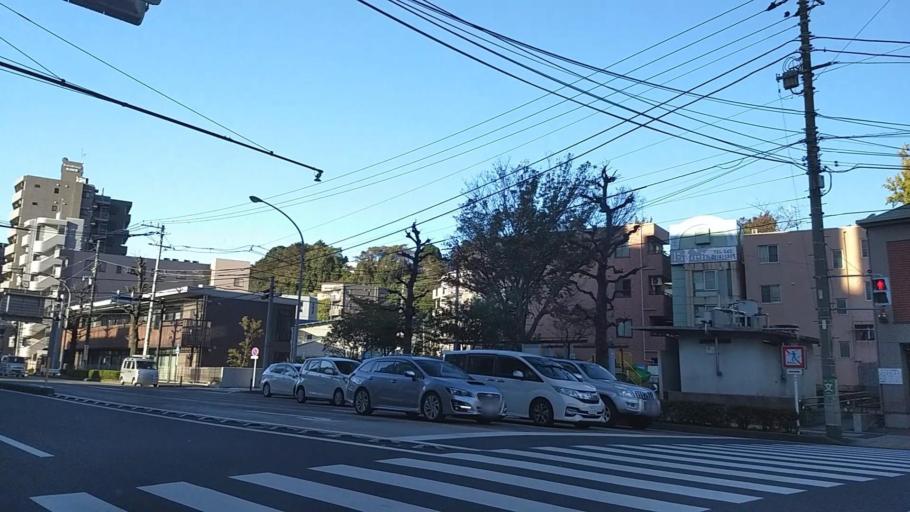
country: JP
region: Kanagawa
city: Yokohama
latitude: 35.4652
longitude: 139.6120
